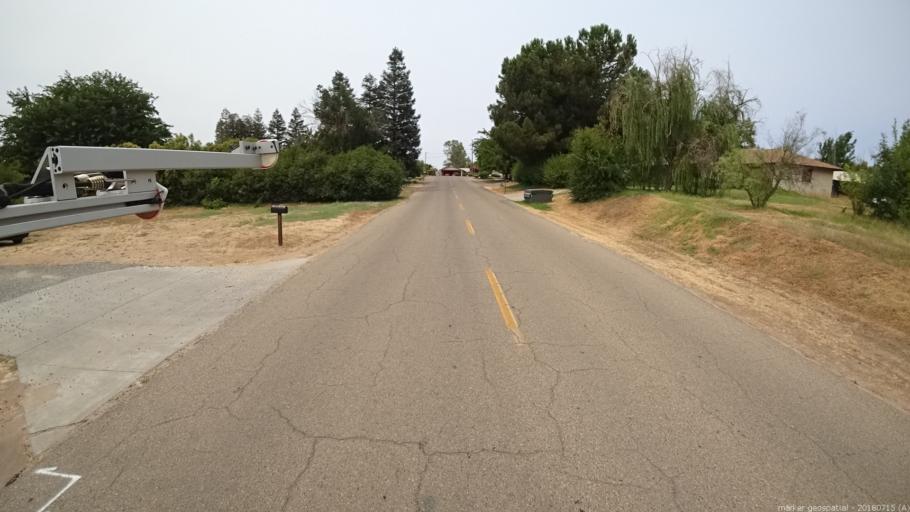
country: US
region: California
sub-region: Madera County
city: Madera Acres
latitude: 37.0100
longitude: -120.0845
